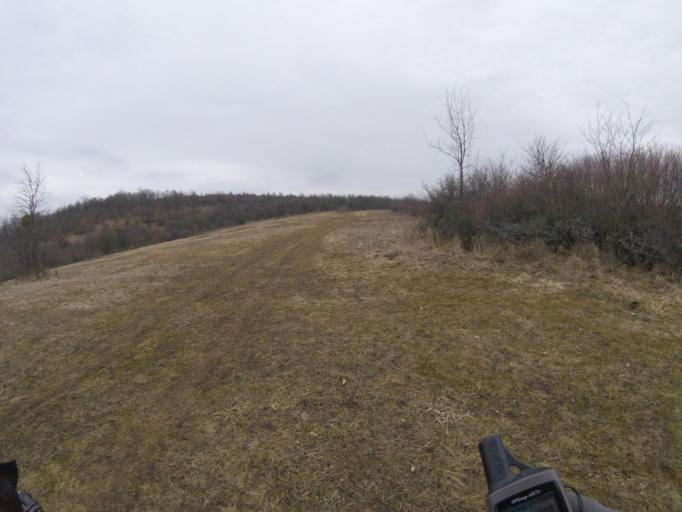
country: HU
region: Borsod-Abauj-Zemplen
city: Rudabanya
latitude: 48.4635
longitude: 20.6011
